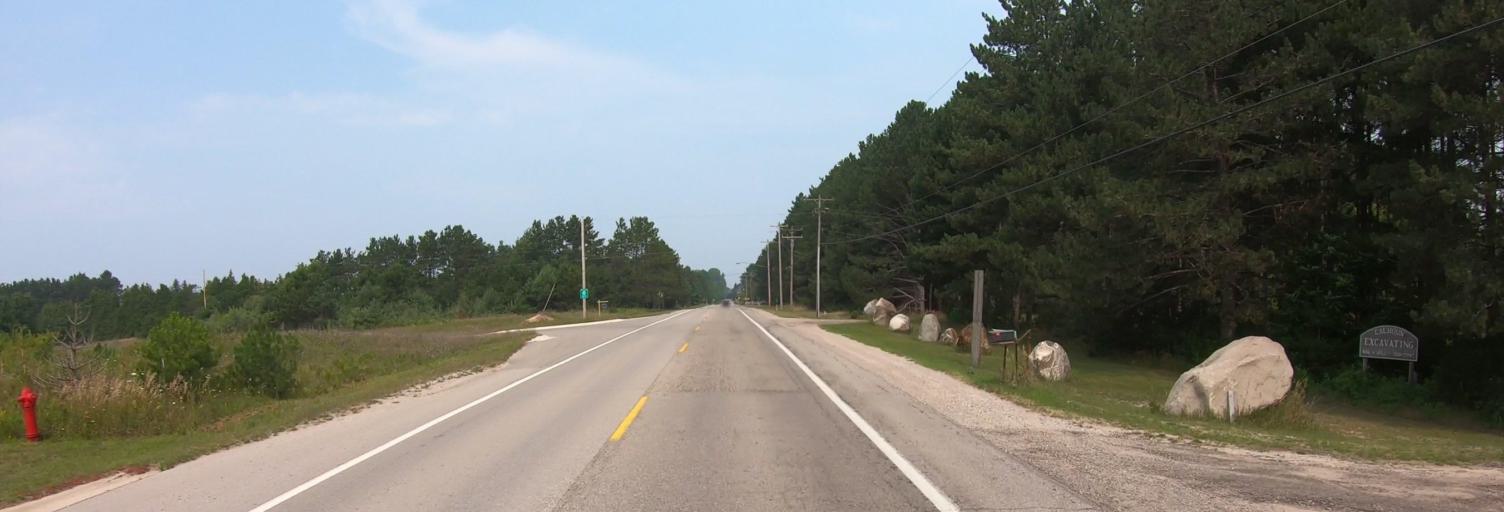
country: US
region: Michigan
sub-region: Leelanau County
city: Leland
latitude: 45.1378
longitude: -85.6154
